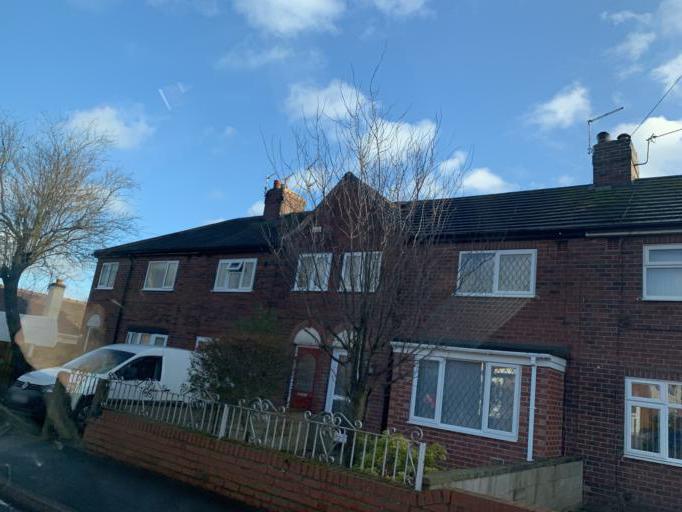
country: GB
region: England
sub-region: City and Borough of Wakefield
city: Knottingley
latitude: 53.7108
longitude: -1.2653
